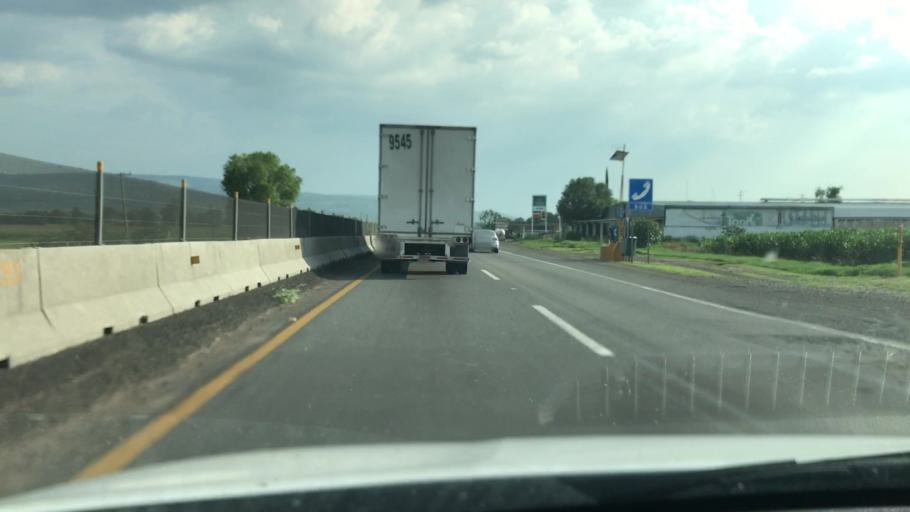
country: MX
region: Guanajuato
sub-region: Abasolo
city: San Bernardo Pena Blanca
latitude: 20.4884
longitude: -101.4895
